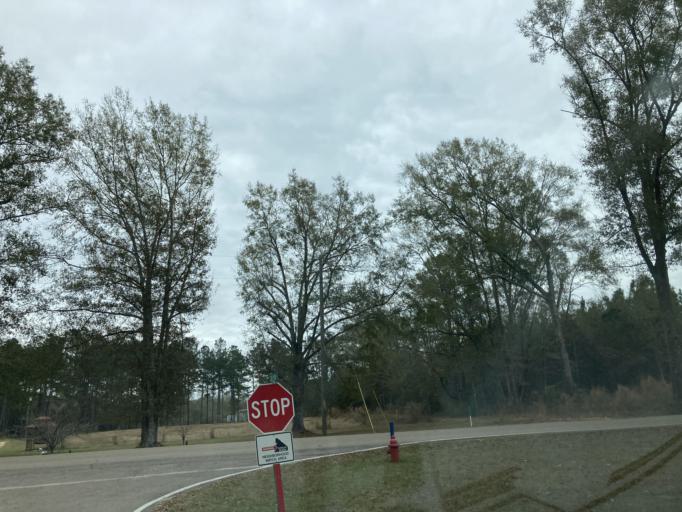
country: US
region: Mississippi
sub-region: Forrest County
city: Hattiesburg
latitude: 31.1640
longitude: -89.2187
